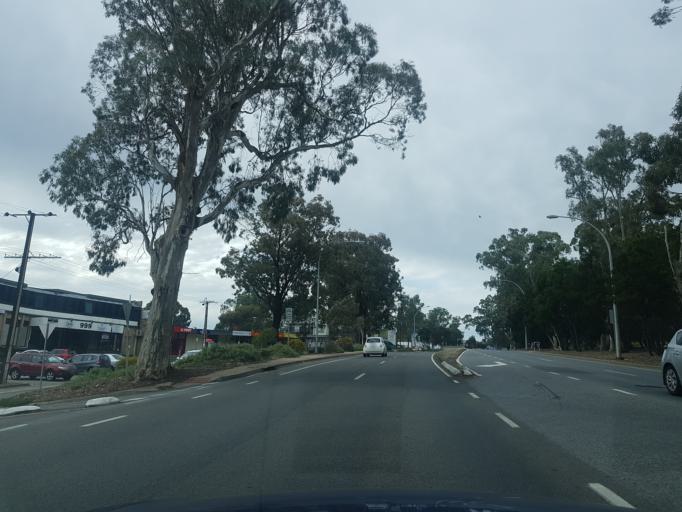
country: AU
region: South Australia
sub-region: Campbelltown
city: Athelstone
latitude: -34.8538
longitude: 138.6981
